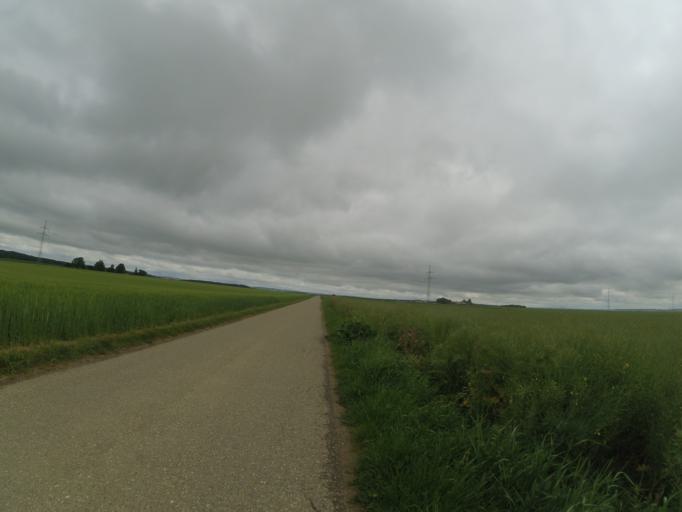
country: DE
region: Baden-Wuerttemberg
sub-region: Tuebingen Region
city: Bernstadt
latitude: 48.4651
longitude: 10.0443
